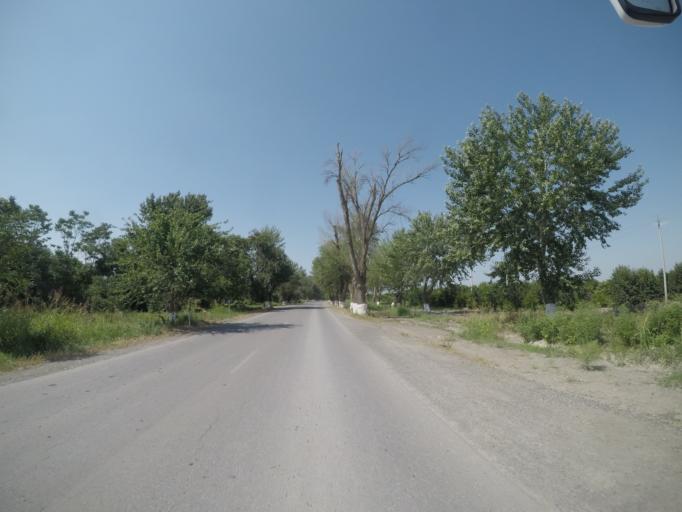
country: AZ
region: Agdas
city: Agdas
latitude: 40.6938
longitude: 47.5390
